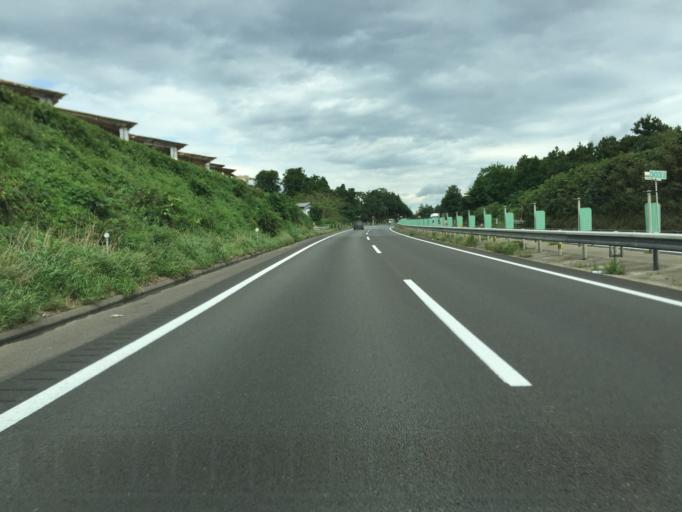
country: JP
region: Miyagi
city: Shiroishi
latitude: 38.0643
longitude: 140.6544
